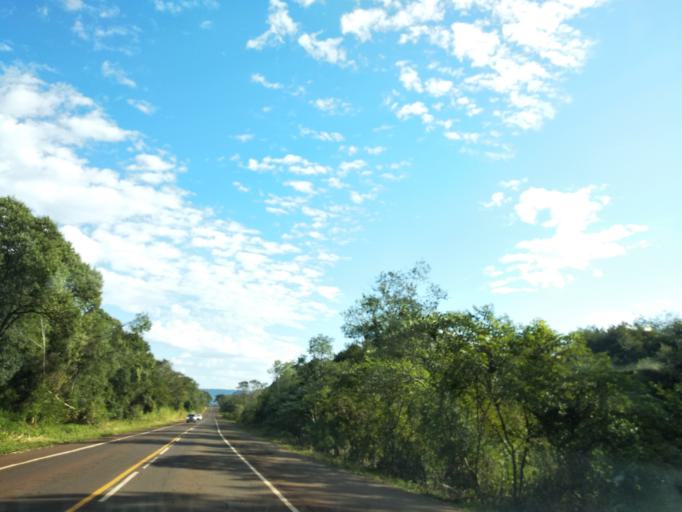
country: AR
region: Misiones
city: Aristobulo del Valle
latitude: -27.0934
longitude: -54.9516
